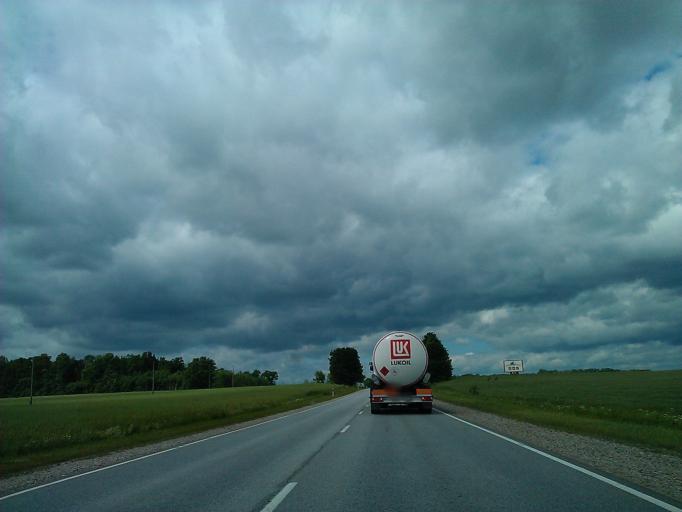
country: LV
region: Engure
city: Smarde
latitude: 56.9176
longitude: 23.3177
